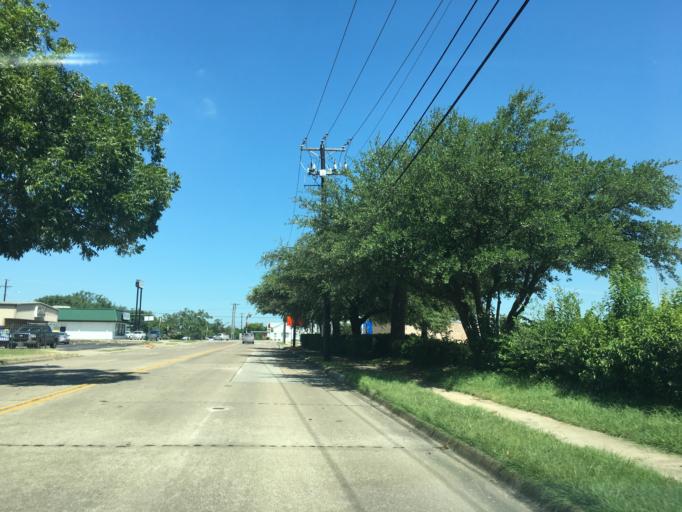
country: US
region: Texas
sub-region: Dallas County
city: Garland
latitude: 32.8435
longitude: -96.6881
